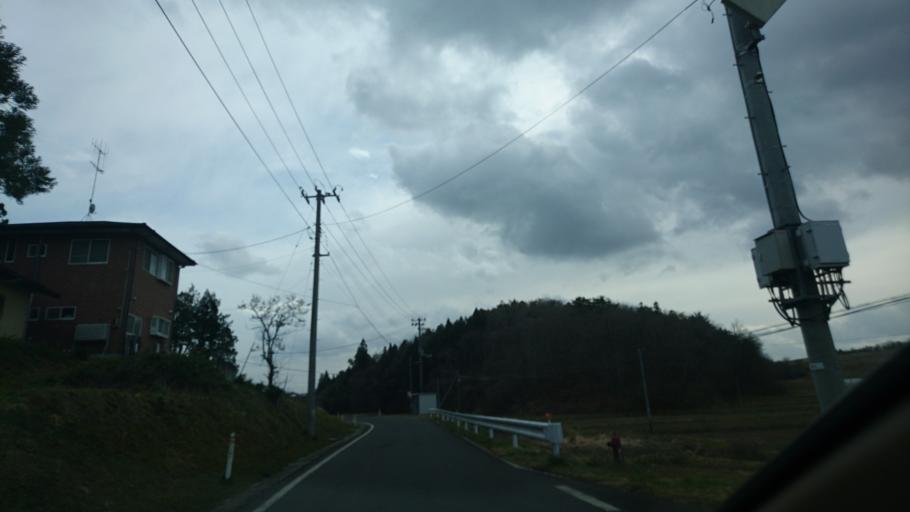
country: JP
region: Iwate
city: Ichinoseki
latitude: 38.8931
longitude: 141.1691
